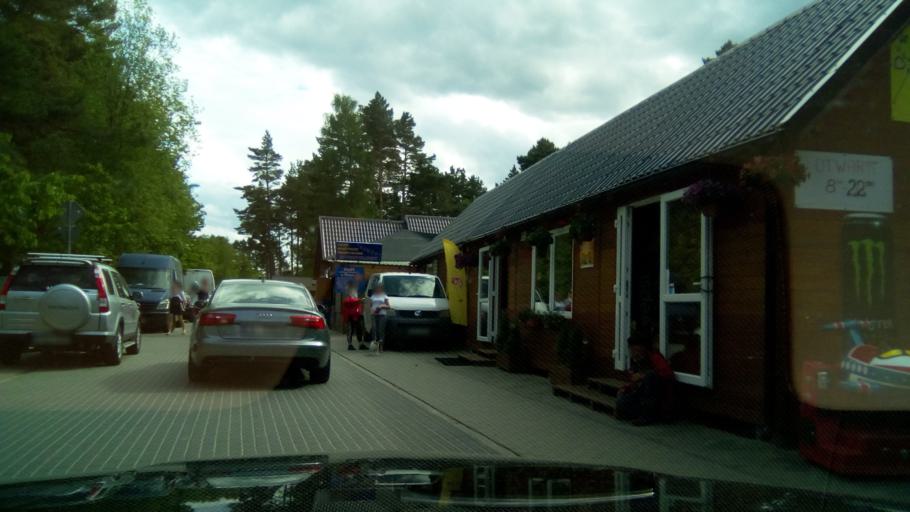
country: PL
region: Pomeranian Voivodeship
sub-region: Powiat pucki
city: Wierzchucino
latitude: 54.8301
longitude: 18.0762
